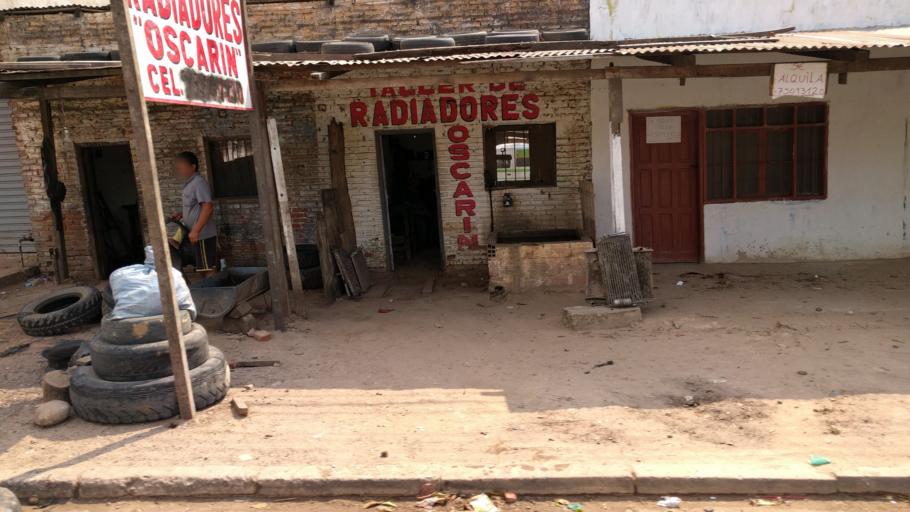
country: BO
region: Santa Cruz
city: Santiago del Torno
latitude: -18.0009
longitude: -63.3877
